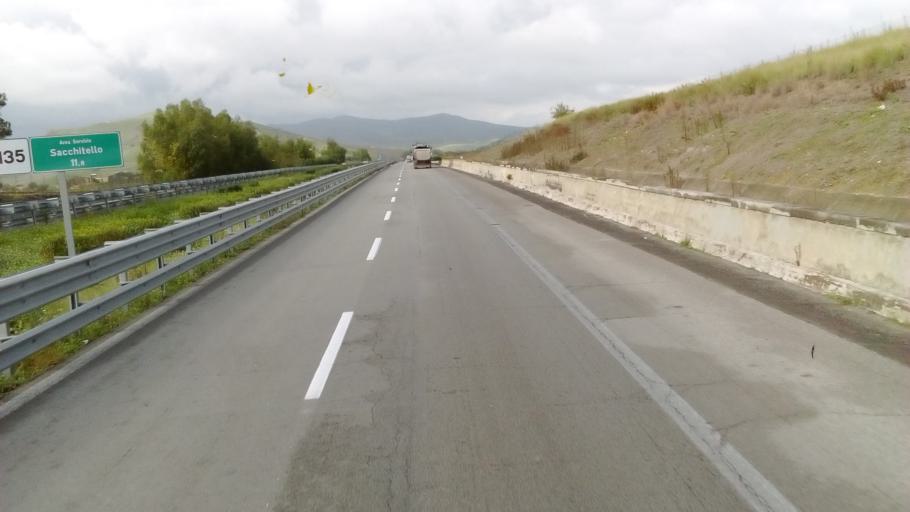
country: IT
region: Sicily
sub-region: Enna
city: Assoro
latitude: 37.5721
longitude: 14.4610
